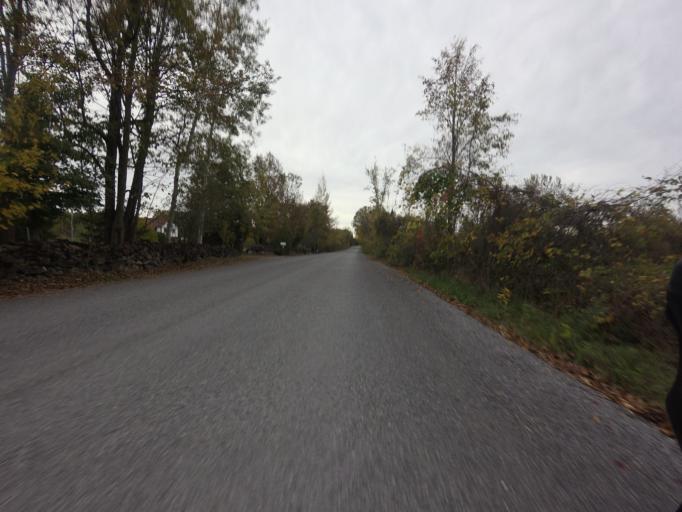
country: CA
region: Ontario
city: Bells Corners
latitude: 45.0801
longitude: -75.7572
